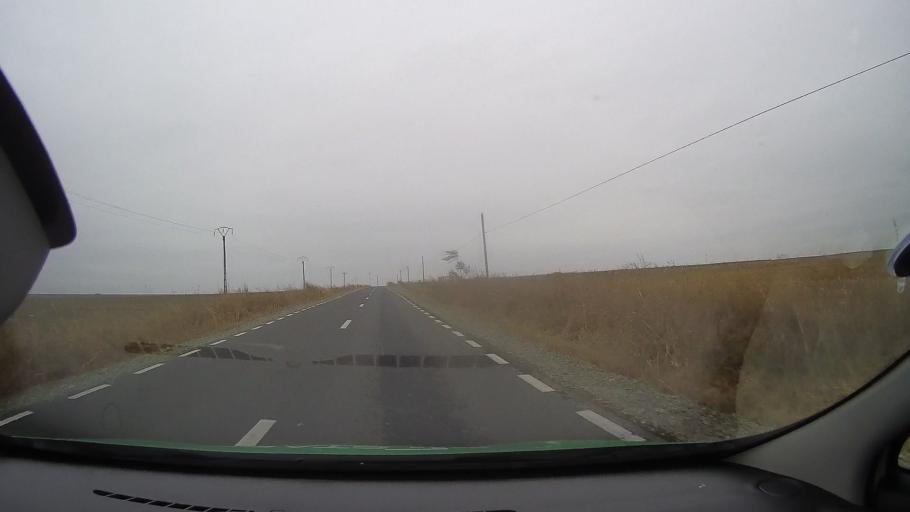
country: RO
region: Constanta
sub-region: Comuna Tortoman
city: Tortoman
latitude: 44.3544
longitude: 28.2137
